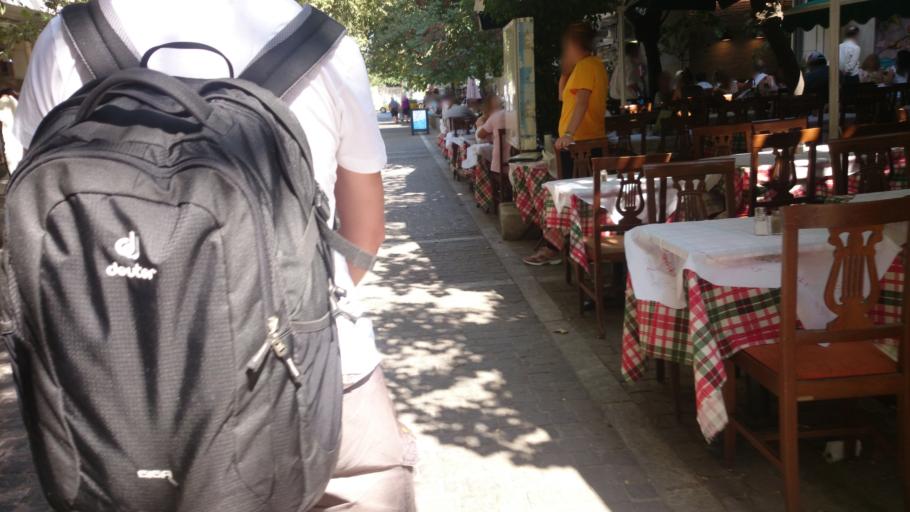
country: GR
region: Attica
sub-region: Nomarchia Athinas
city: Athens
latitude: 37.9697
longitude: 23.7304
